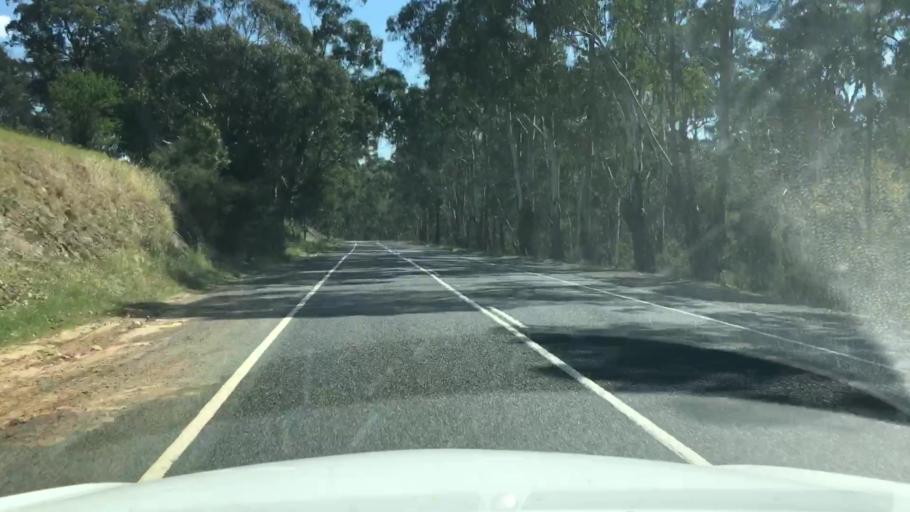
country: AU
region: Victoria
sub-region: Nillumbik
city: Saint Andrews
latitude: -37.6578
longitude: 145.2730
